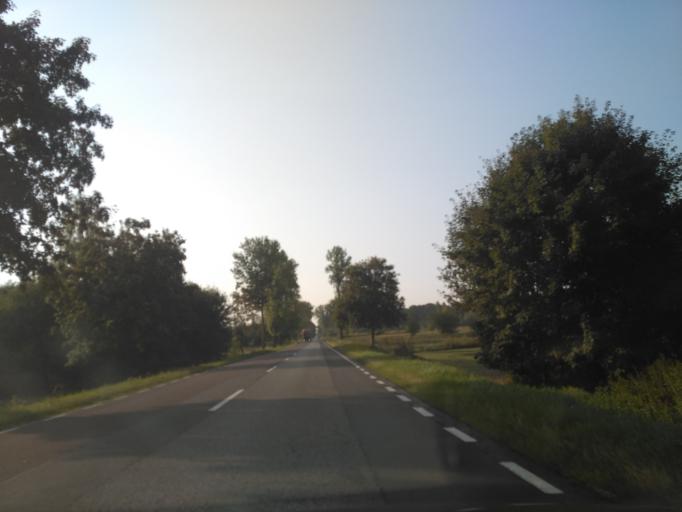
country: PL
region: Lublin Voivodeship
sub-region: Powiat krasnicki
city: Szastarka
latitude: 50.8704
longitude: 22.2712
